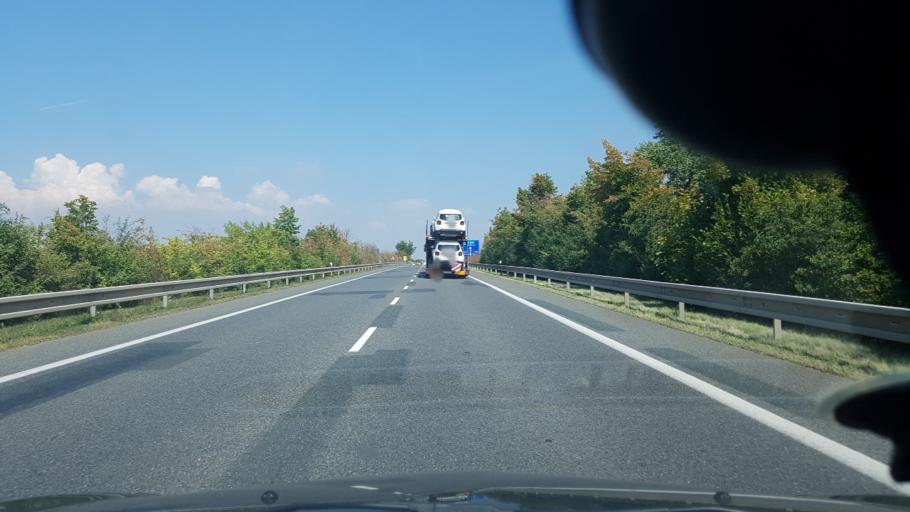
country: CZ
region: South Moravian
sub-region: Okres Breclav
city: Dolni Dunajovice
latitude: 48.8467
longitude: 16.6106
